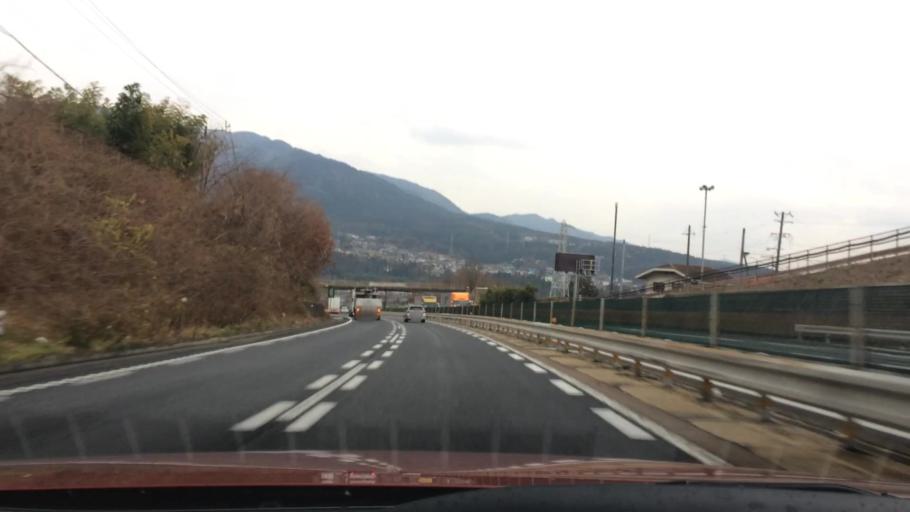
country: JP
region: Gifu
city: Nakatsugawa
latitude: 35.4852
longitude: 137.5116
